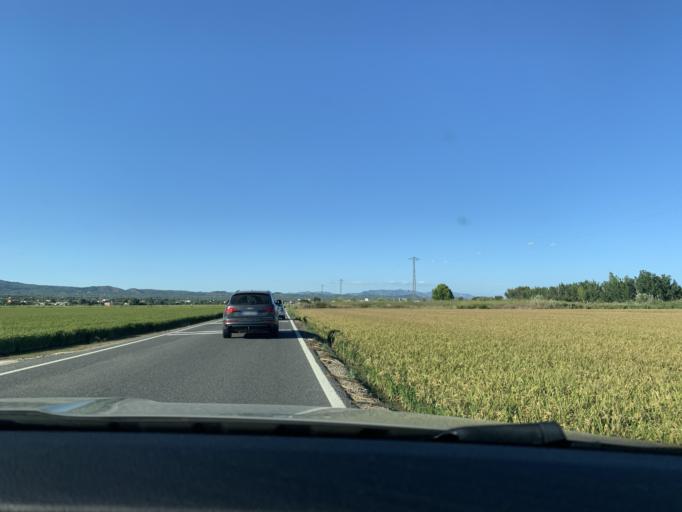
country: ES
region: Catalonia
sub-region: Provincia de Tarragona
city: Camarles
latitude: 40.7768
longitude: 0.6893
